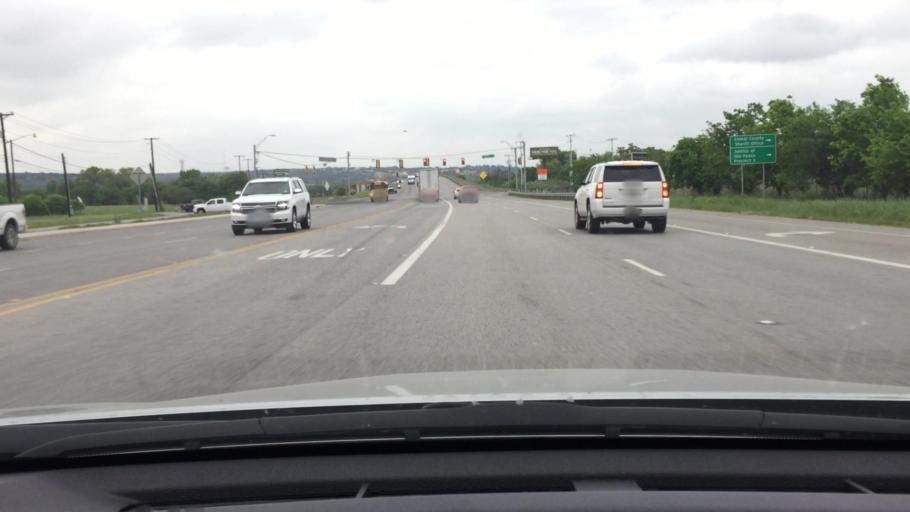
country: US
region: Texas
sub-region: Comal County
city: New Braunfels
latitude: 29.6775
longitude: -98.1550
